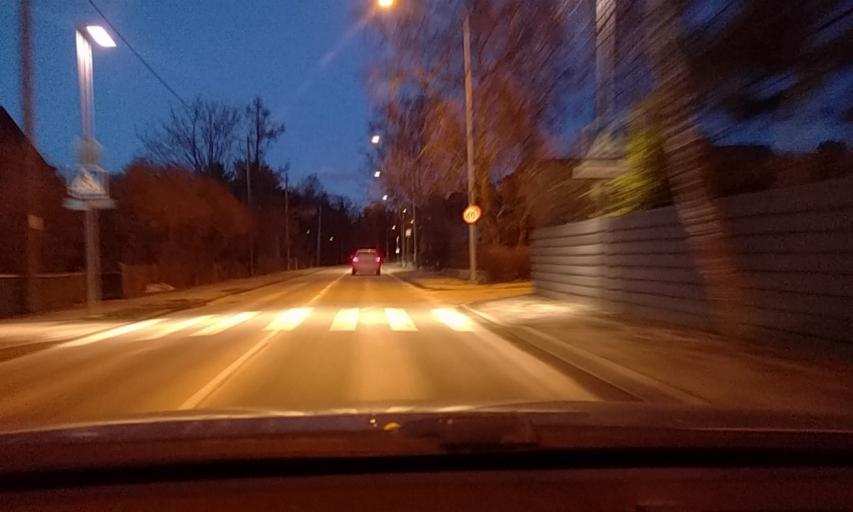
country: EE
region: Harju
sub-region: Viimsi vald
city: Viimsi
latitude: 59.4833
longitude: 24.8597
